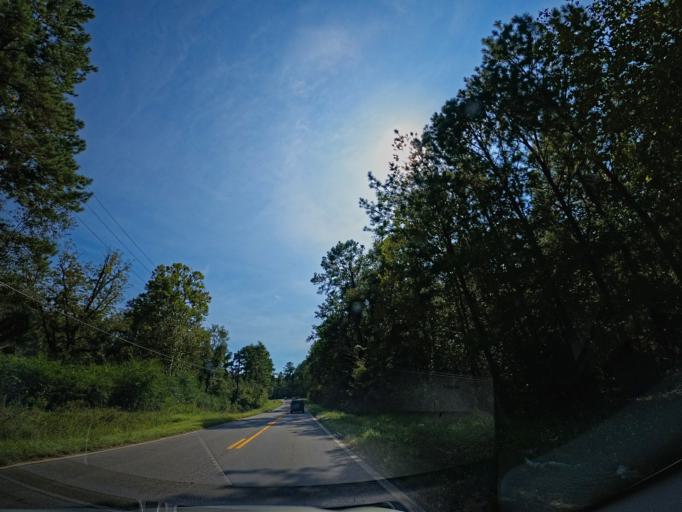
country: US
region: Florida
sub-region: Okaloosa County
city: Crestview
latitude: 30.7380
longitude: -86.6235
